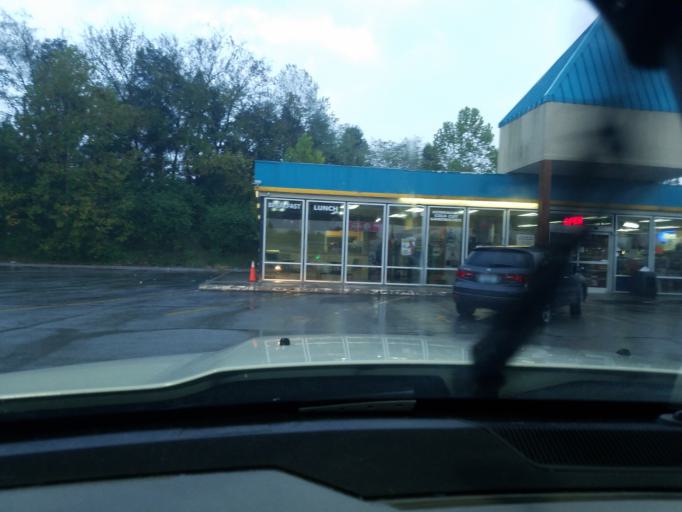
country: US
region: Kentucky
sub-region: Franklin County
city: Frankfort
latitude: 38.1417
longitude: -84.9889
